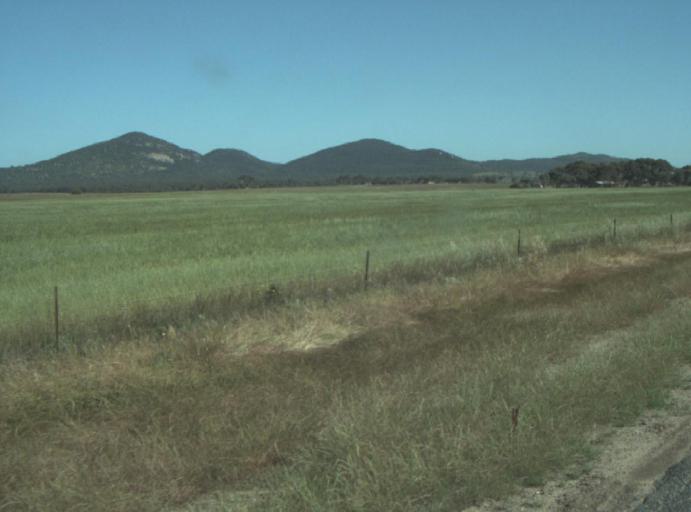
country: AU
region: Victoria
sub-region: Wyndham
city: Little River
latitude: -37.9830
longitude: 144.4595
